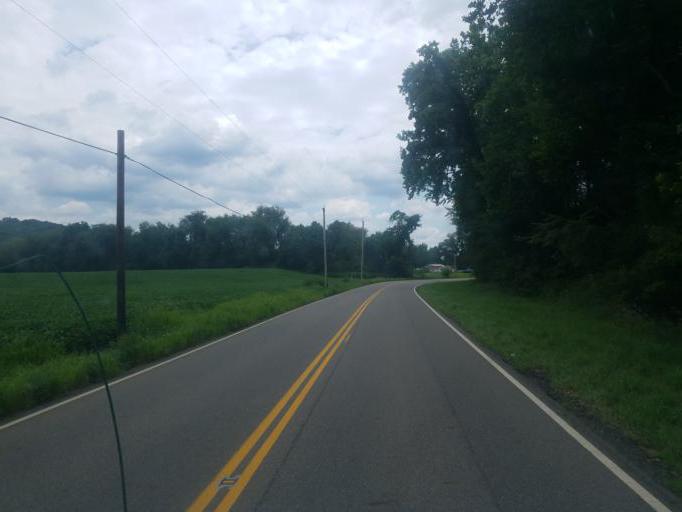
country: US
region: Ohio
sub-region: Licking County
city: Utica
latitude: 40.1544
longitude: -82.4525
